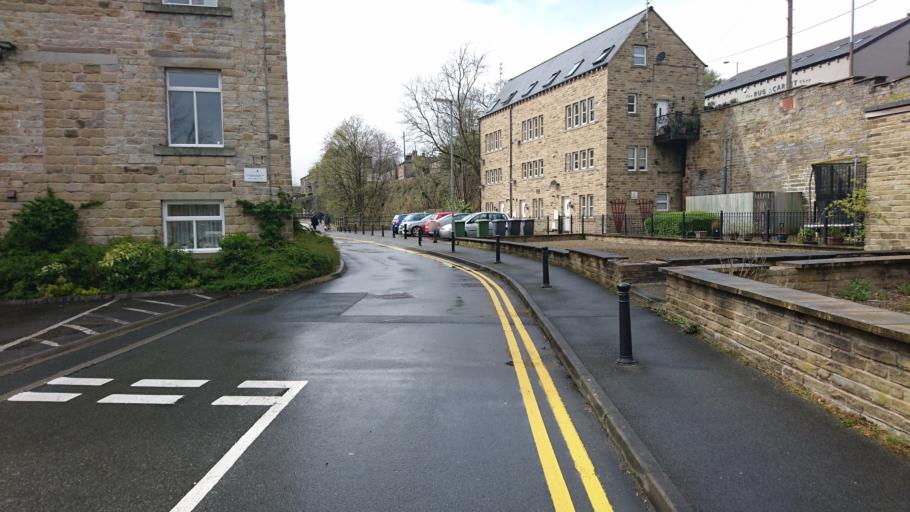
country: GB
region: England
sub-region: Kirklees
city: Holmfirth
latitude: 53.5687
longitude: -1.7904
